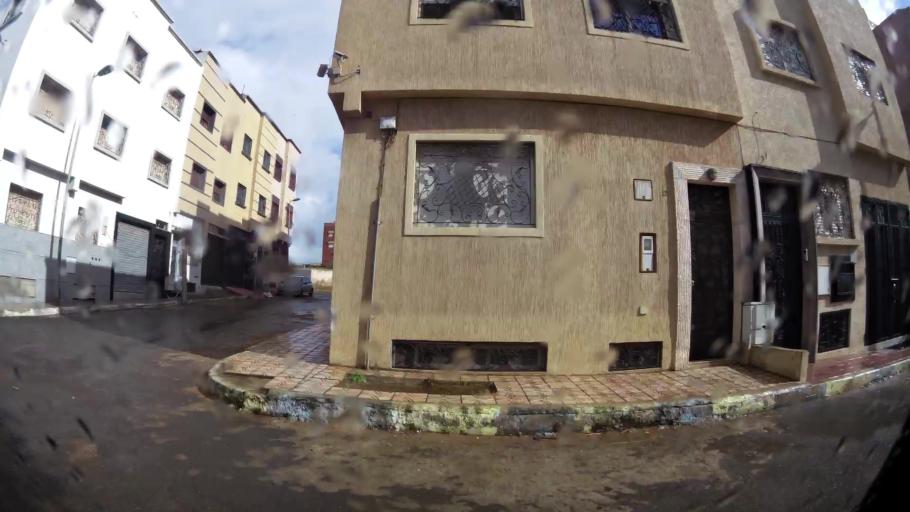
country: MA
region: Grand Casablanca
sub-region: Casablanca
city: Casablanca
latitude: 33.5633
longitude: -7.6961
